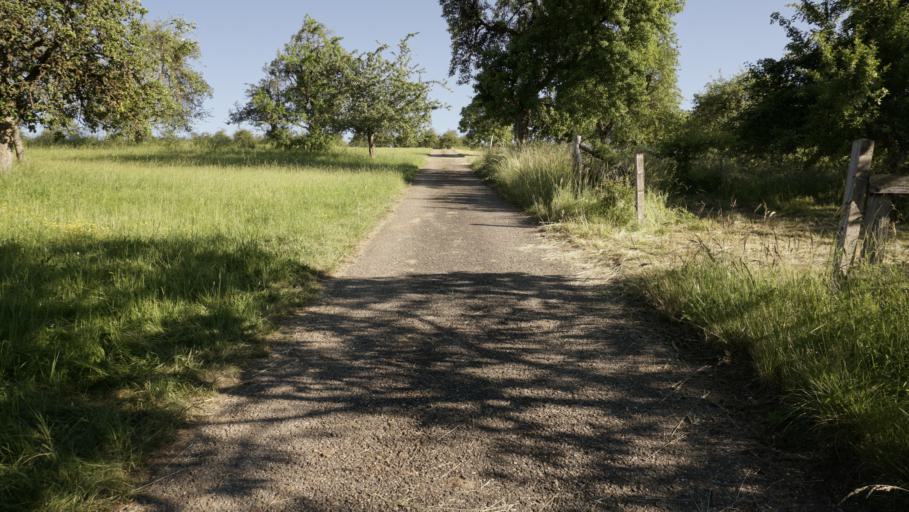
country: DE
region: Baden-Wuerttemberg
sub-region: Karlsruhe Region
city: Billigheim
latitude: 49.3789
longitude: 9.2102
